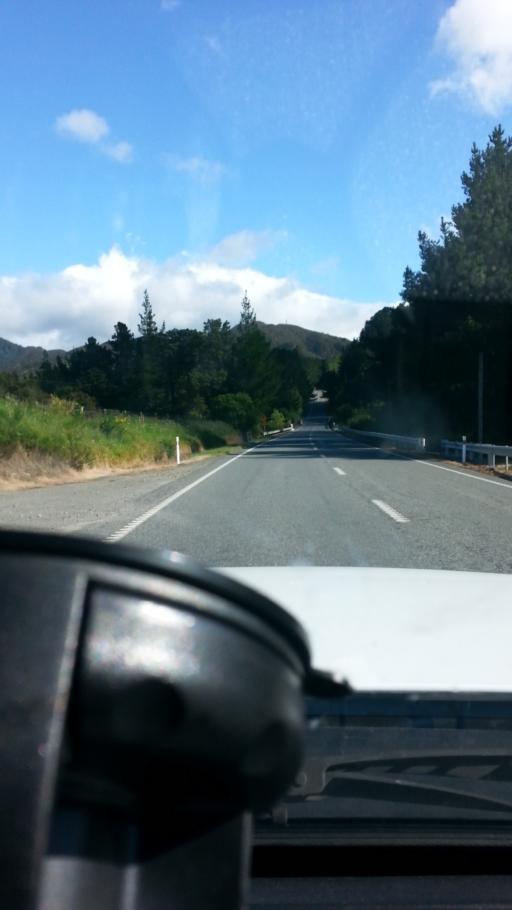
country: NZ
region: Wellington
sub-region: Masterton District
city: Masterton
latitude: -40.7646
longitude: 175.6074
